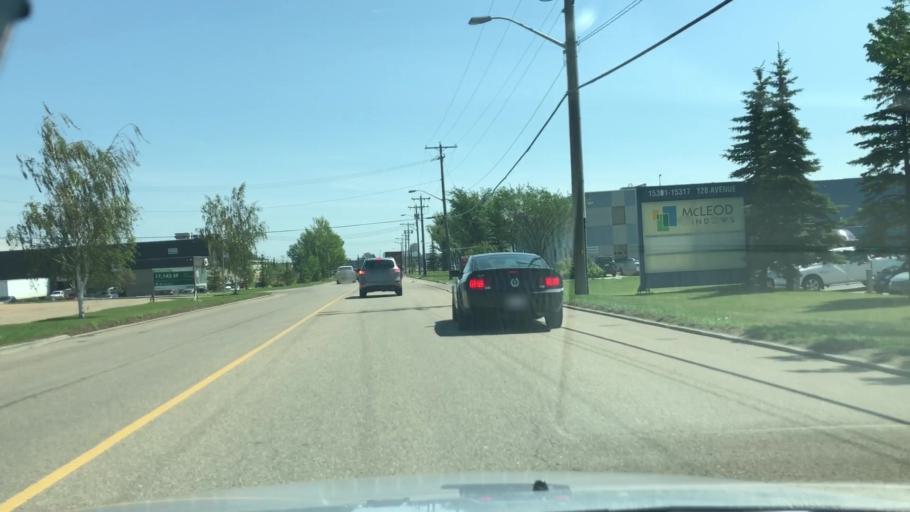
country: CA
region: Alberta
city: St. Albert
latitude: 53.5848
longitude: -113.5862
